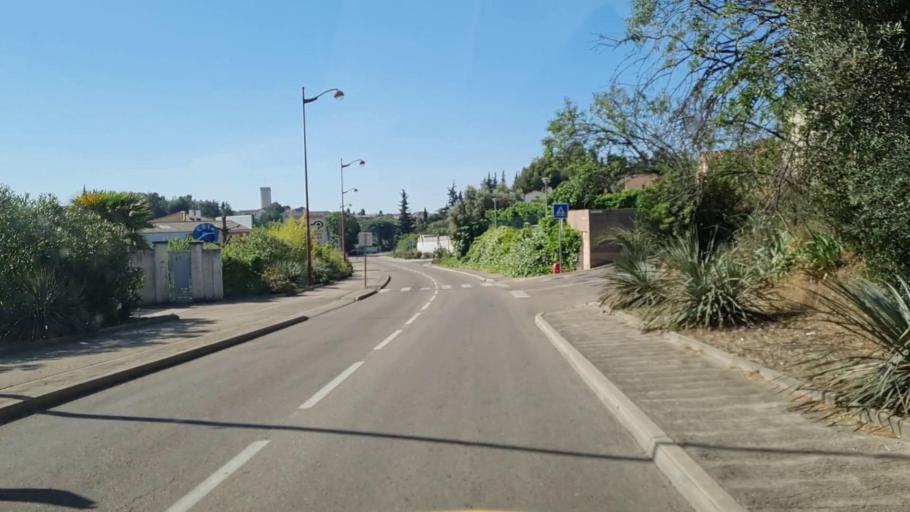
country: FR
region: Languedoc-Roussillon
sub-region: Departement du Gard
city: Saint-Gilles
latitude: 43.6862
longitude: 4.4286
